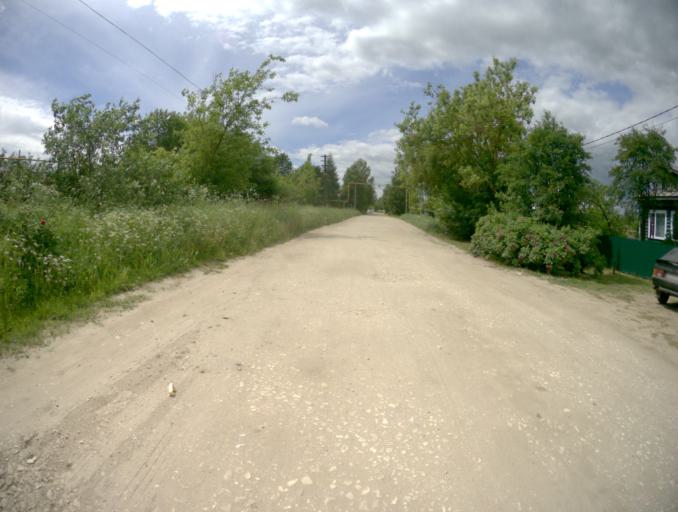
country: RU
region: Ivanovo
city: Savino
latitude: 56.5894
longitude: 41.2179
